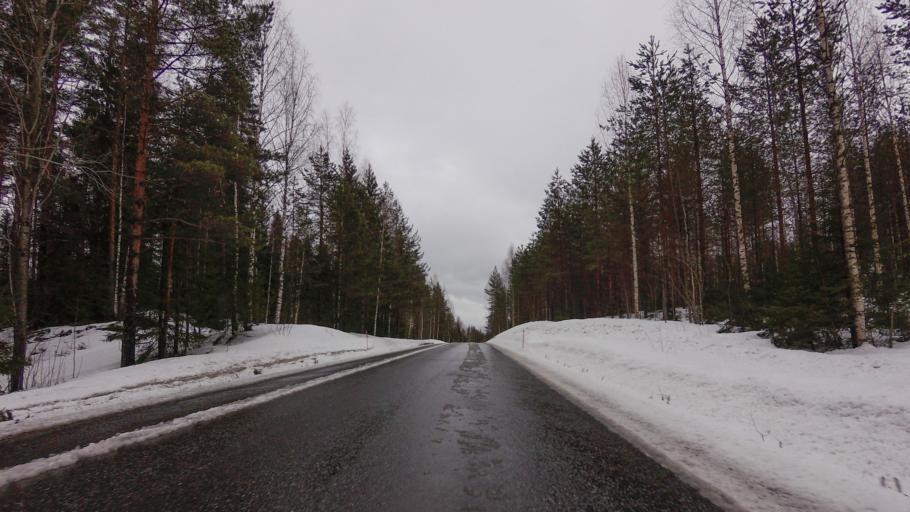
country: FI
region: Southern Savonia
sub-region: Savonlinna
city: Savonlinna
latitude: 61.9849
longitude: 28.7991
